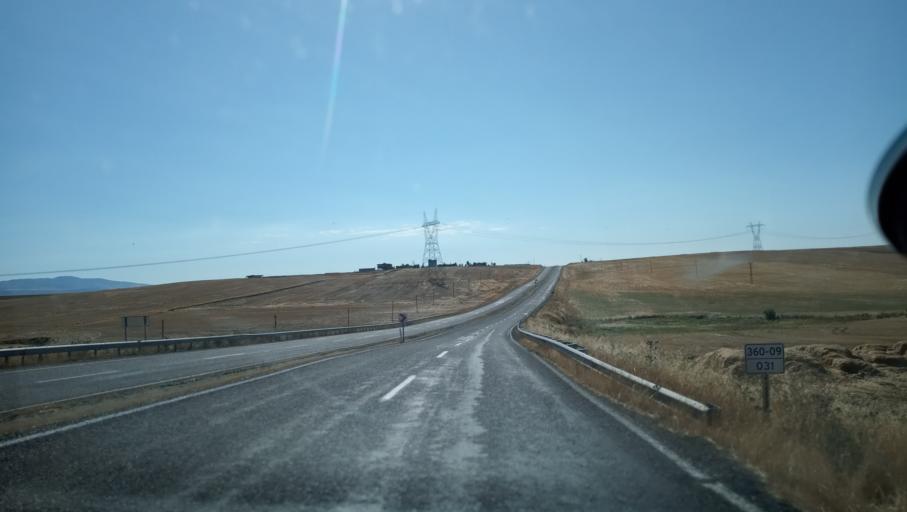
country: TR
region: Diyarbakir
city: Bagdere
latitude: 38.1309
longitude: 40.7653
